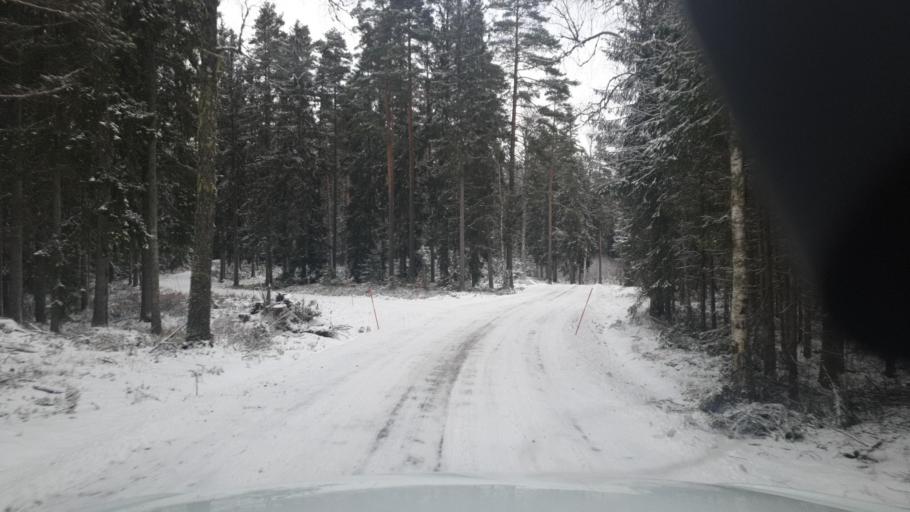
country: SE
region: Vaermland
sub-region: Karlstads Kommun
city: Edsvalla
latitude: 59.4612
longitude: 13.1010
